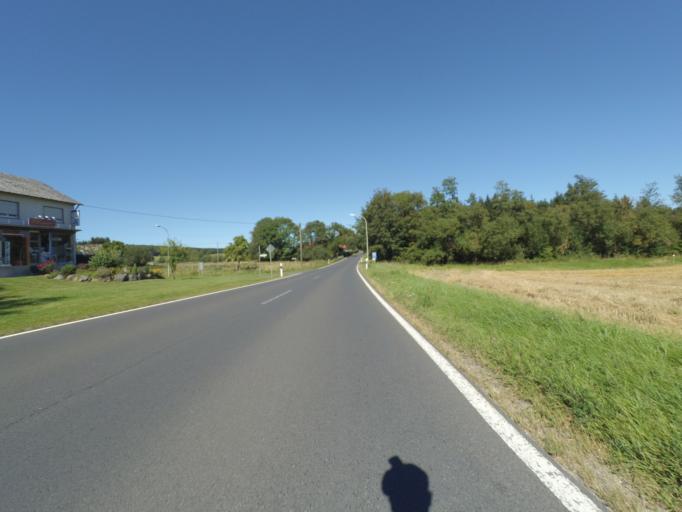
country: DE
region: Rheinland-Pfalz
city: Uxheim
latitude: 50.3242
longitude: 6.7343
